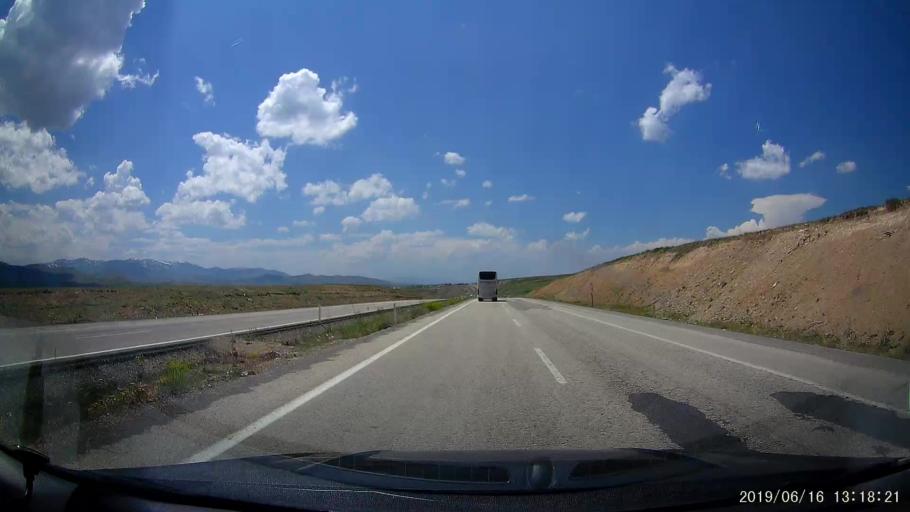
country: TR
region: Agri
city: Taslicay
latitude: 39.6303
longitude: 43.4325
